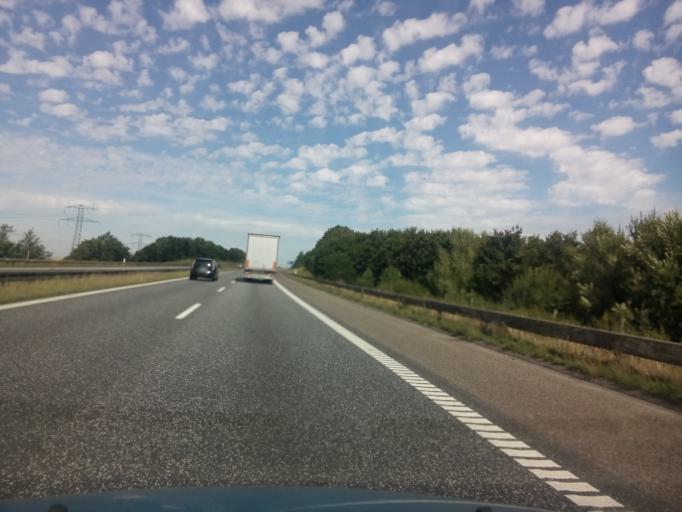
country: DK
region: Central Jutland
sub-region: Arhus Kommune
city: Trige
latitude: 56.3000
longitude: 10.1267
